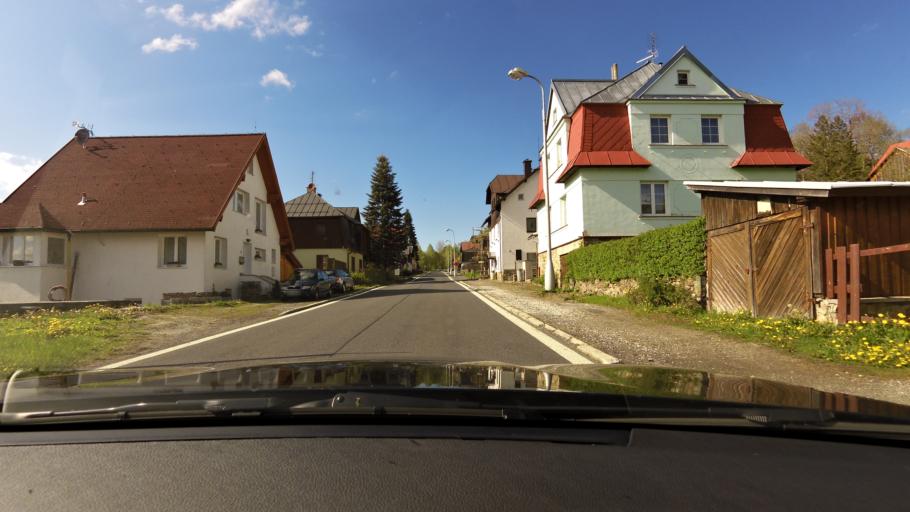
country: CZ
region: Plzensky
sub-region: Okres Klatovy
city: Zelezna Ruda
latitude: 49.1391
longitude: 13.2291
